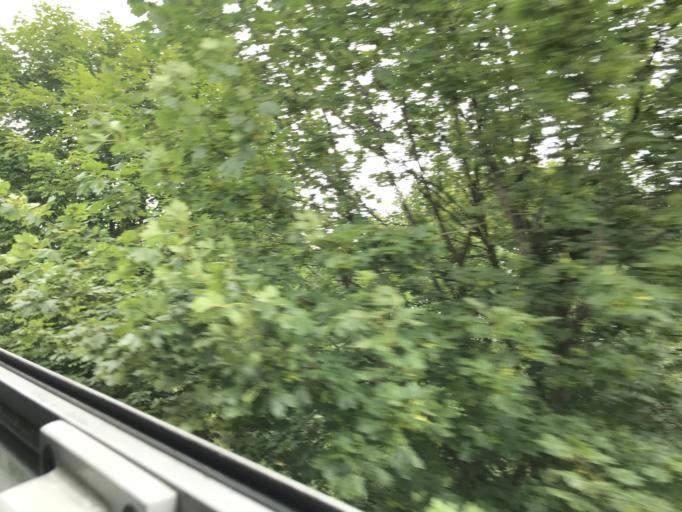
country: PL
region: Pomeranian Voivodeship
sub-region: Powiat malborski
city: Malbork
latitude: 54.0461
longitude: 19.0272
